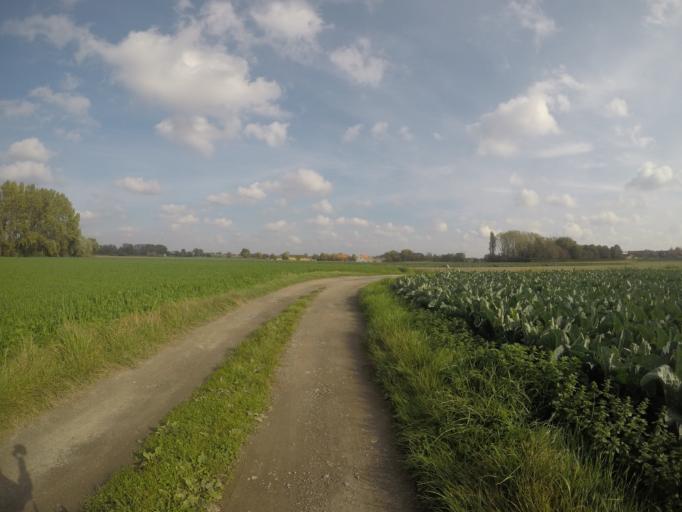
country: BE
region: Flanders
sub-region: Provincie West-Vlaanderen
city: Moorslede
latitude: 50.8489
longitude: 3.0671
